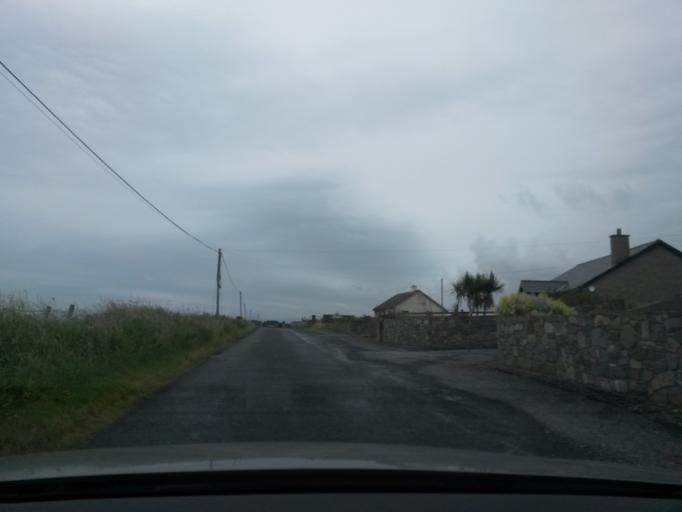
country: IE
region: Connaught
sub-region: Sligo
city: Strandhill
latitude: 54.2554
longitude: -8.8046
